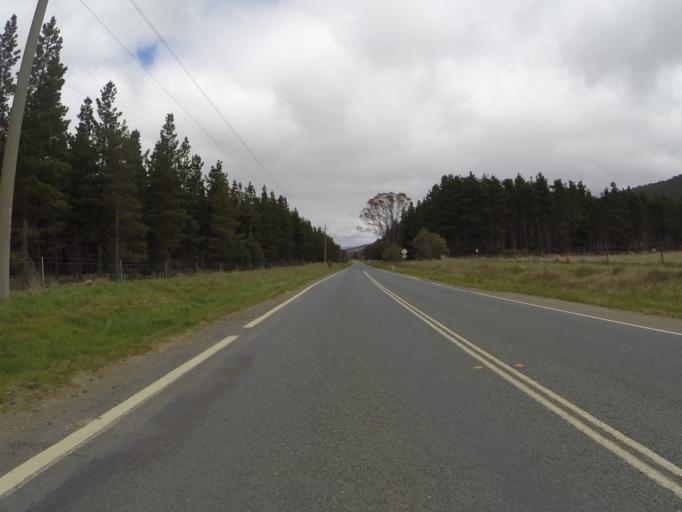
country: AU
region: Australian Capital Territory
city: Canberra
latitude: -35.2380
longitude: 149.1972
